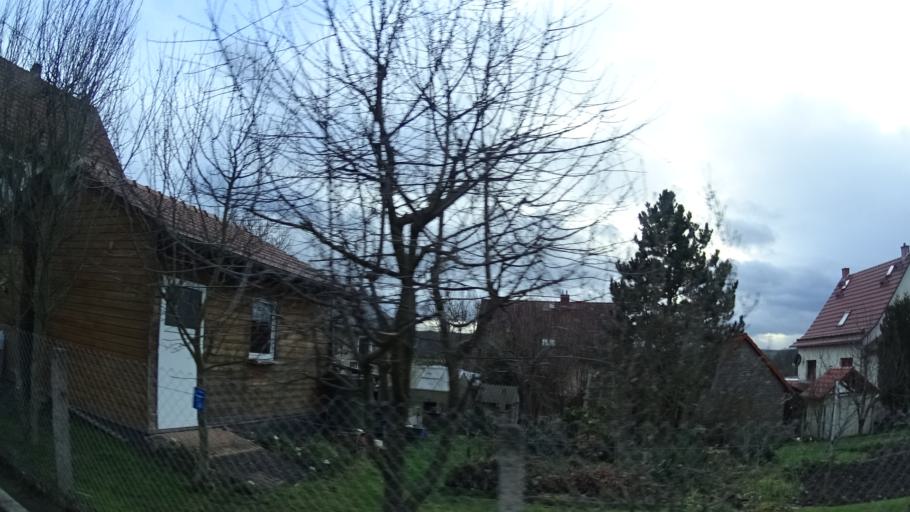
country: DE
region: Thuringia
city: Bibra
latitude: 50.8136
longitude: 11.5494
